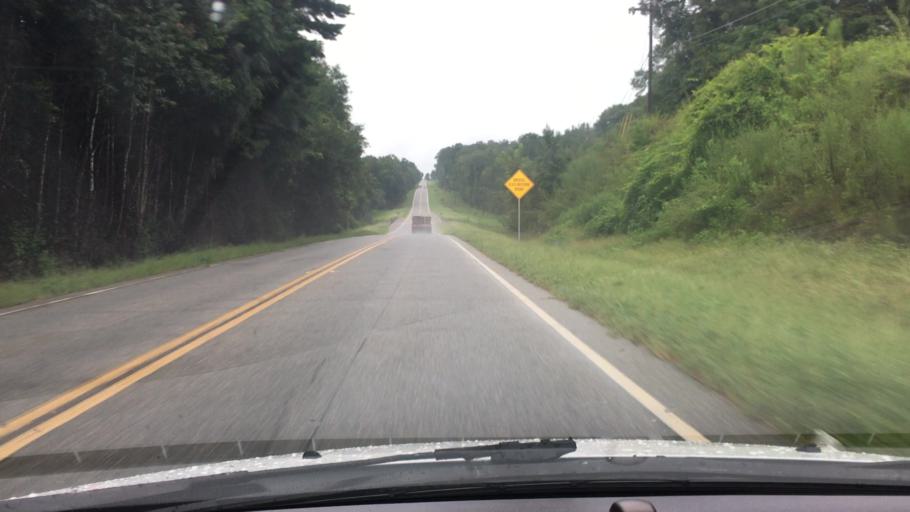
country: US
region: Georgia
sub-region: Grady County
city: Cairo
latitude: 30.8154
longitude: -84.2514
